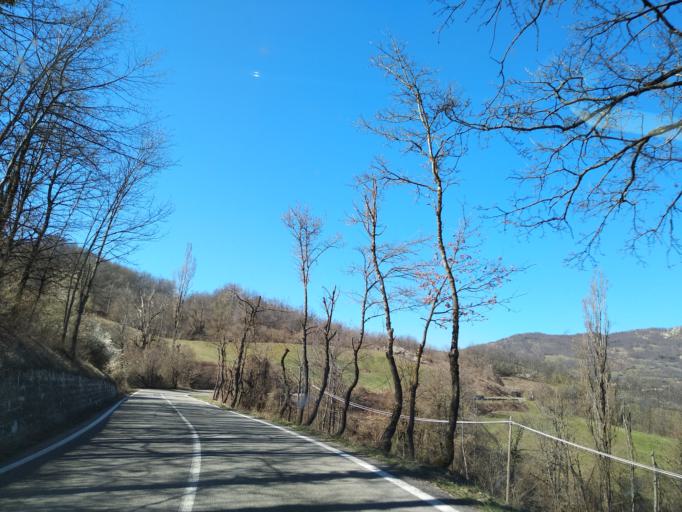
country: IT
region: Emilia-Romagna
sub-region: Provincia di Reggio Emilia
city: Ramiseto
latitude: 44.4144
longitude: 10.2938
